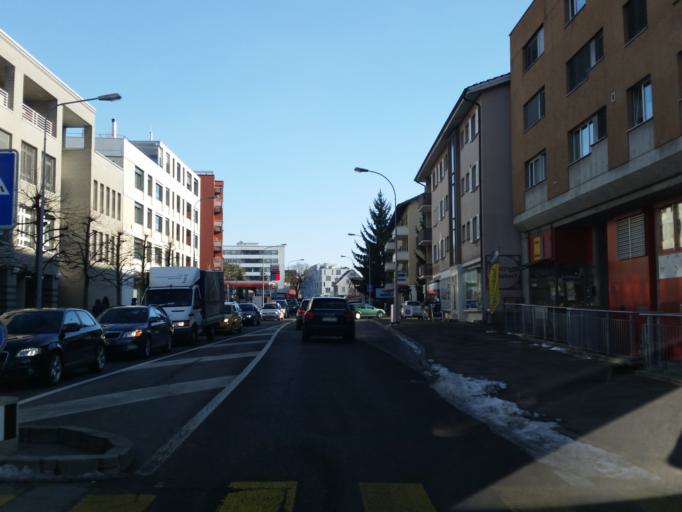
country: CH
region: Aargau
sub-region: Bezirk Baden
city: Neuenhof
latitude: 47.4648
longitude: 8.3290
